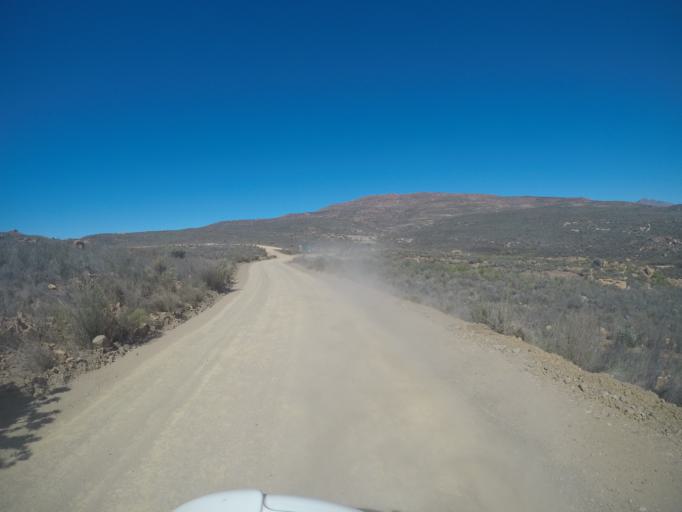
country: ZA
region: Western Cape
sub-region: West Coast District Municipality
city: Clanwilliam
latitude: -32.5063
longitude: 19.2840
